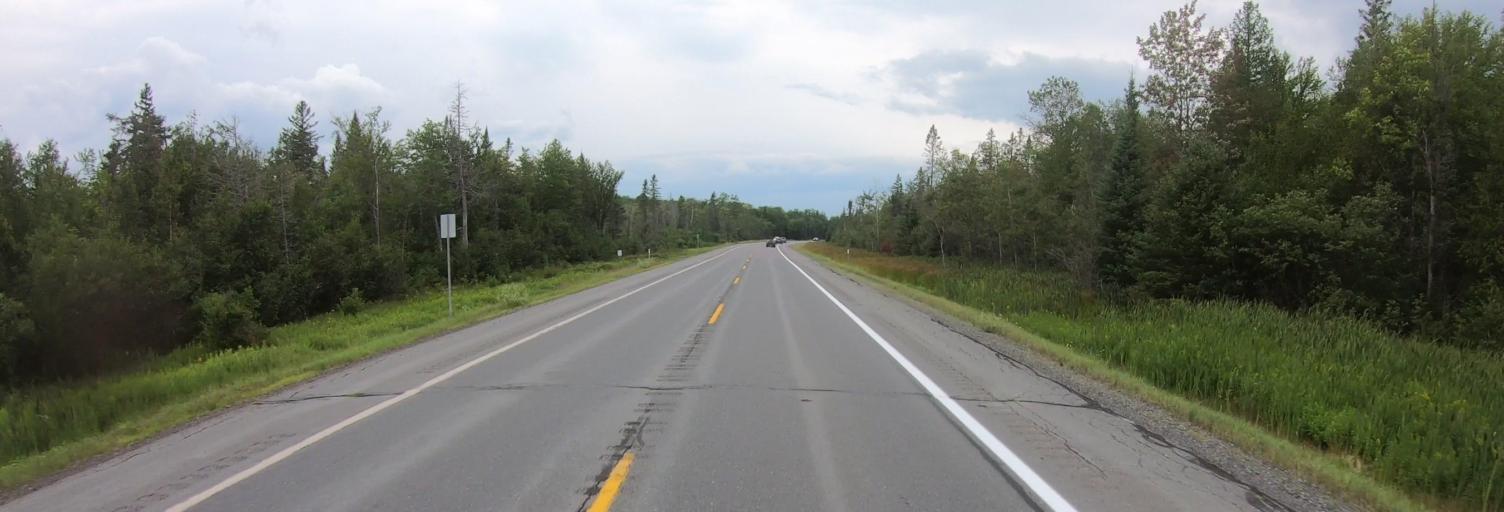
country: US
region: Michigan
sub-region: Baraga County
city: L'Anse
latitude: 46.5817
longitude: -88.4627
